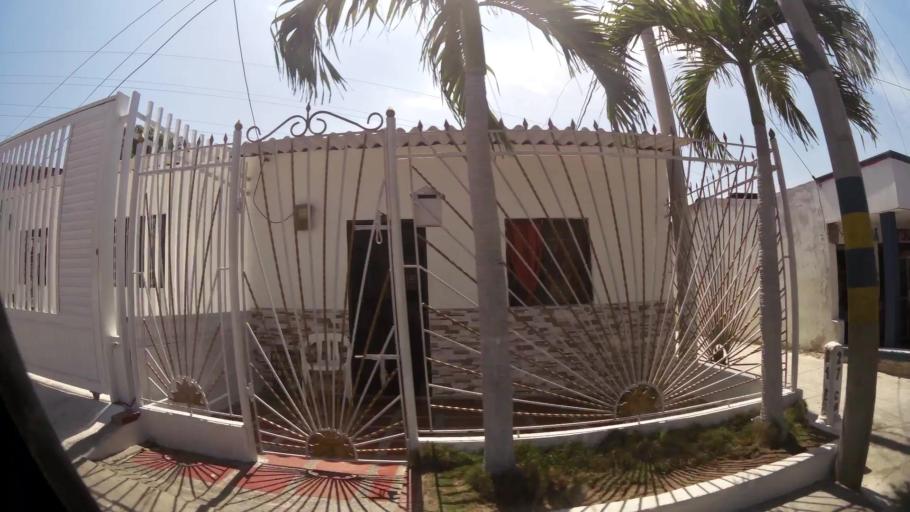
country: CO
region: Atlantico
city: Barranquilla
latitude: 10.9797
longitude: -74.8221
